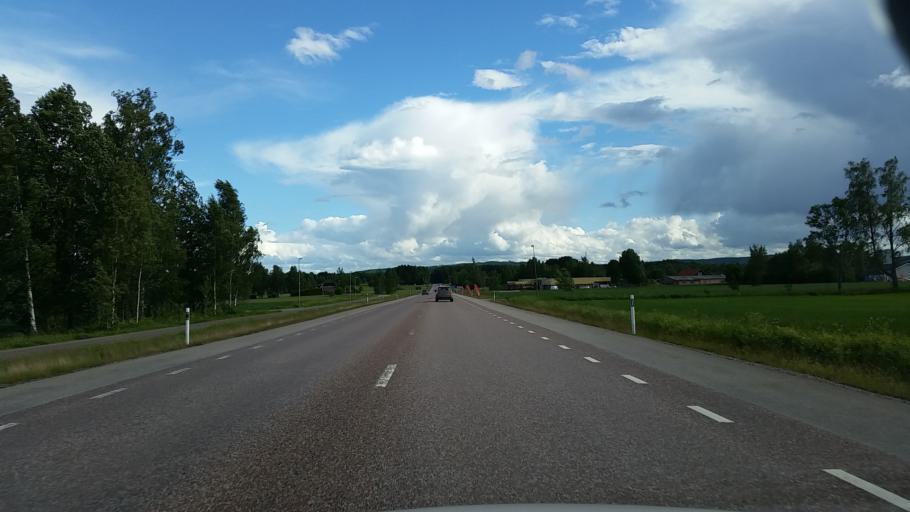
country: SE
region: Dalarna
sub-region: Smedjebackens Kommun
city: Smedjebacken
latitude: 60.0795
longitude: 15.5423
